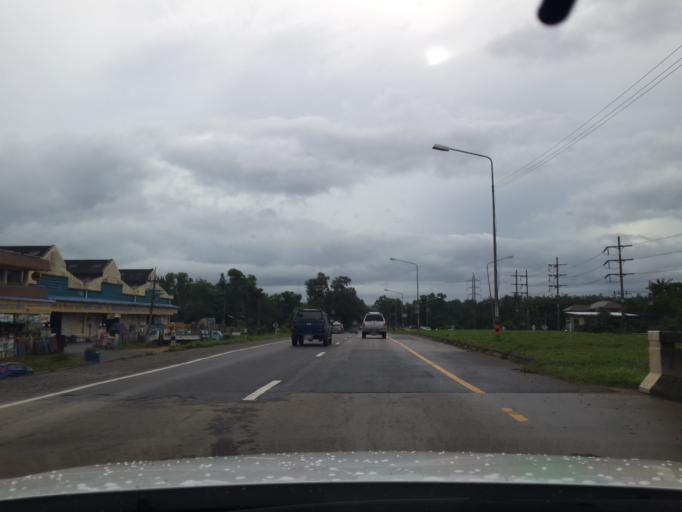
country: TH
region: Songkhla
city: Hat Yai
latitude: 6.9836
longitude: 100.4527
